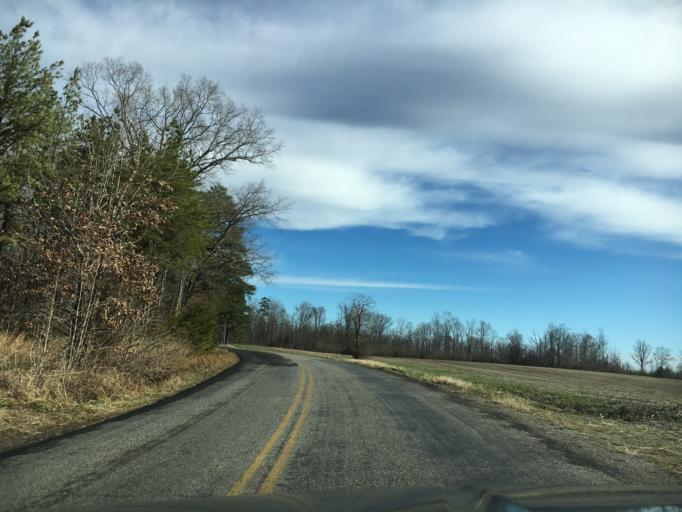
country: US
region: Virginia
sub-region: Nottoway County
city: Crewe
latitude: 37.3142
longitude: -78.1832
